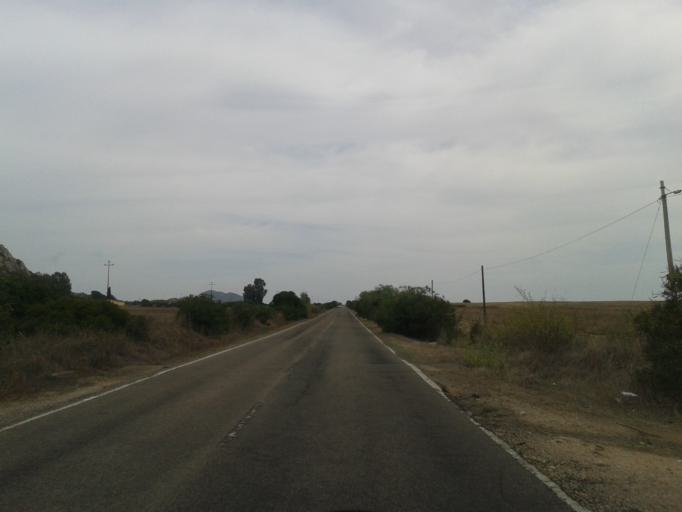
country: IT
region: Sardinia
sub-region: Provincia di Cagliari
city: Olia Speciosa
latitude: 39.2804
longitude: 9.5485
